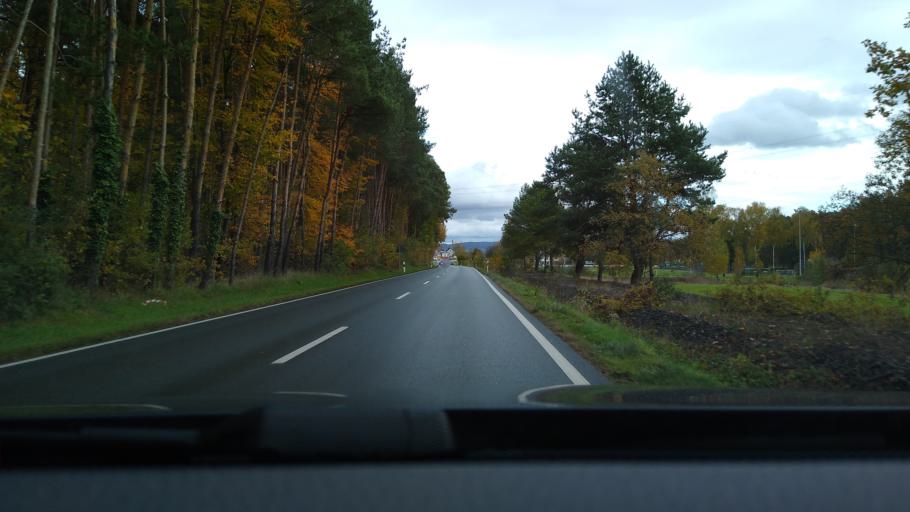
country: DE
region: Bavaria
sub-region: Upper Franconia
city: Hausen
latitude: 49.6925
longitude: 11.0192
